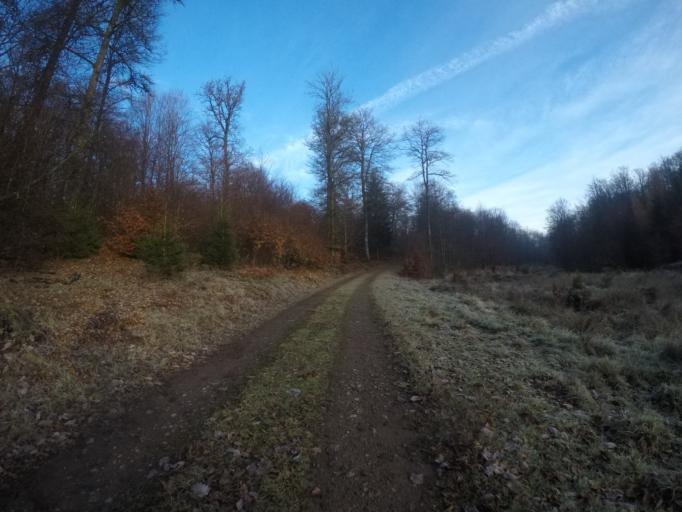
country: BE
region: Wallonia
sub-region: Province du Luxembourg
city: Habay-la-Vieille
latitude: 49.7657
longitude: 5.6582
